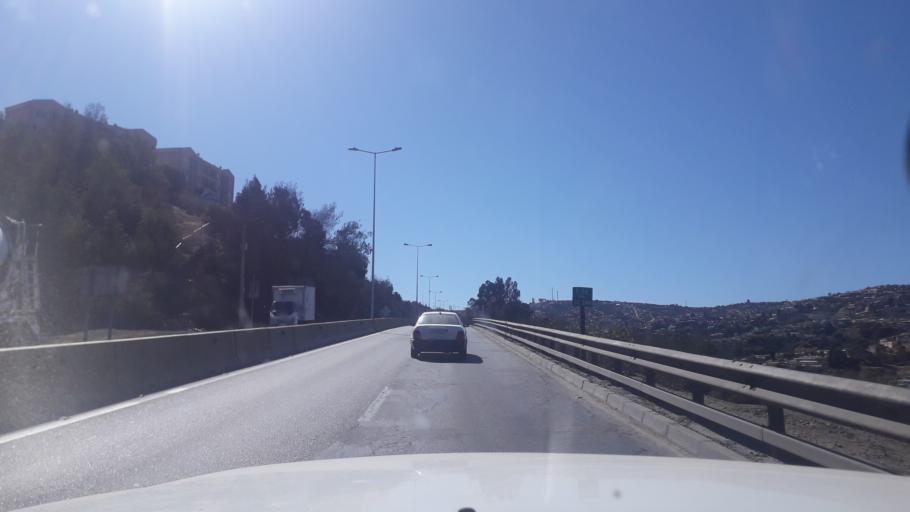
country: CL
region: Valparaiso
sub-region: Provincia de Valparaiso
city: Vina del Mar
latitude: -33.0344
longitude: -71.5013
